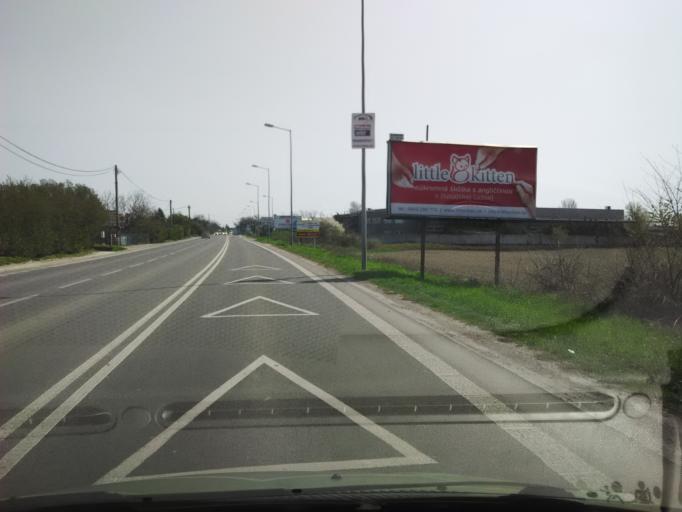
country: SK
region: Bratislavsky
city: Dunajska Luzna
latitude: 48.1227
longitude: 17.2019
